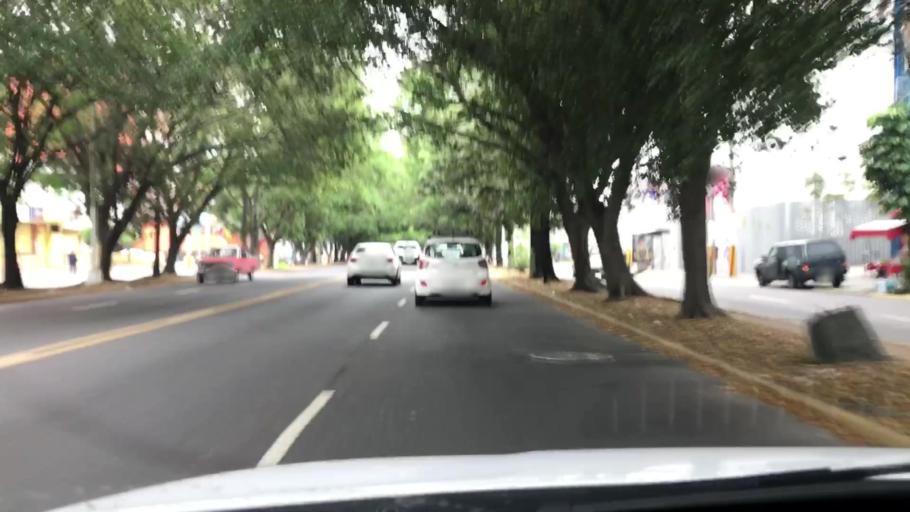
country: MX
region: Jalisco
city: Guadalajara
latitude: 20.6514
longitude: -103.3977
